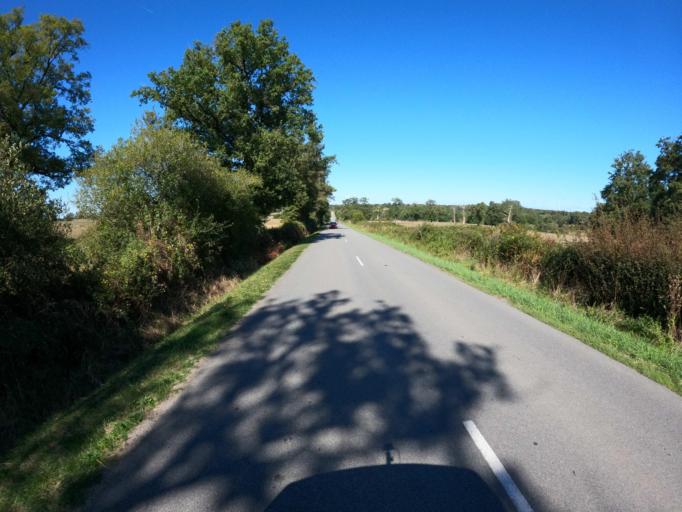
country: FR
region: Limousin
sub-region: Departement de la Haute-Vienne
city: Le Dorat
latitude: 46.2522
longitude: 1.0444
